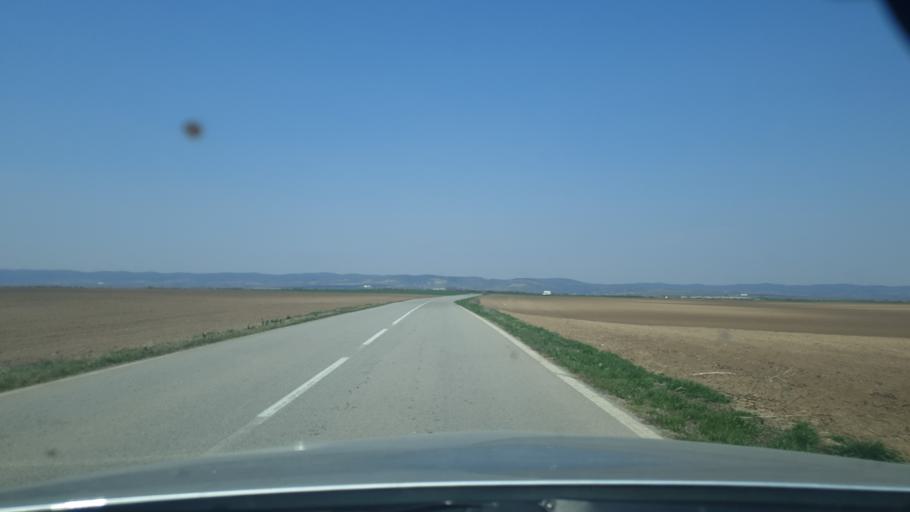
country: RS
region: Autonomna Pokrajina Vojvodina
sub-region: Sremski Okrug
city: Ruma
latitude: 45.0407
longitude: 19.7610
